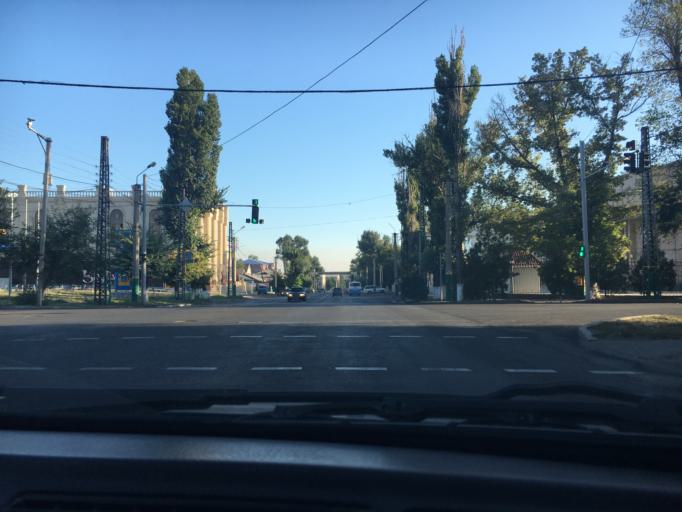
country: KZ
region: Zhambyl
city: Taraz
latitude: 42.8971
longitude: 71.3603
